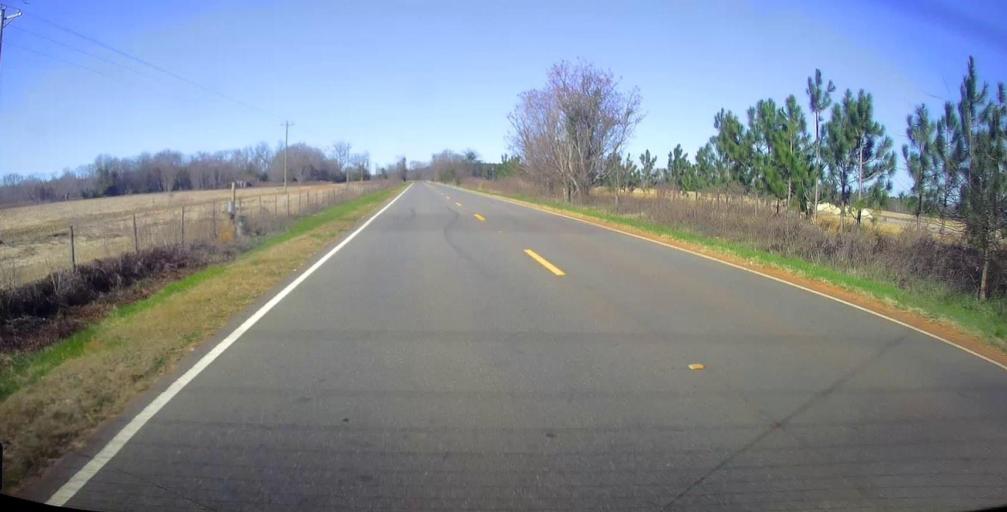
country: US
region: Georgia
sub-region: Macon County
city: Montezuma
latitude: 32.3840
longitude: -84.0154
